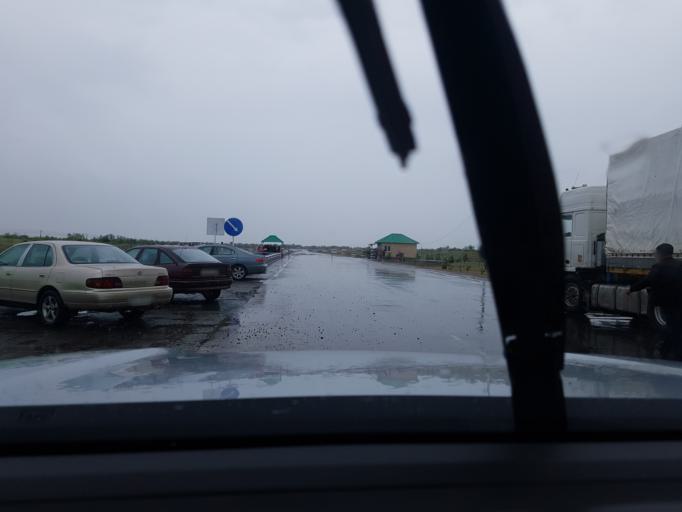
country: TM
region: Lebap
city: Farap
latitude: 39.2075
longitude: 63.7041
